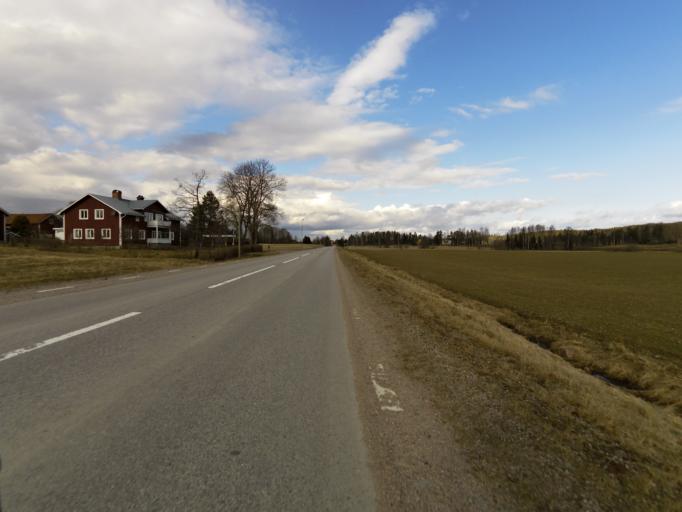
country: SE
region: Dalarna
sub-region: Avesta Kommun
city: Horndal
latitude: 60.4546
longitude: 16.4536
